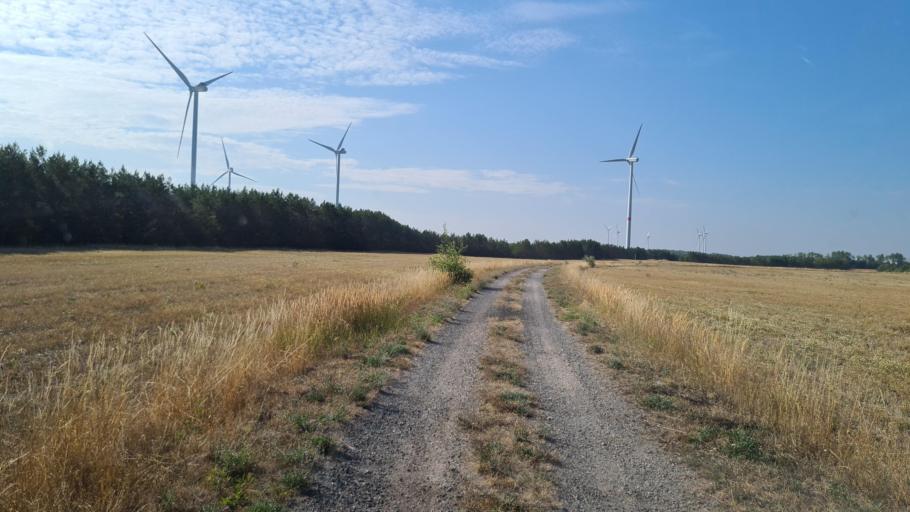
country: DE
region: Brandenburg
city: Sallgast
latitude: 51.5589
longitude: 13.8426
